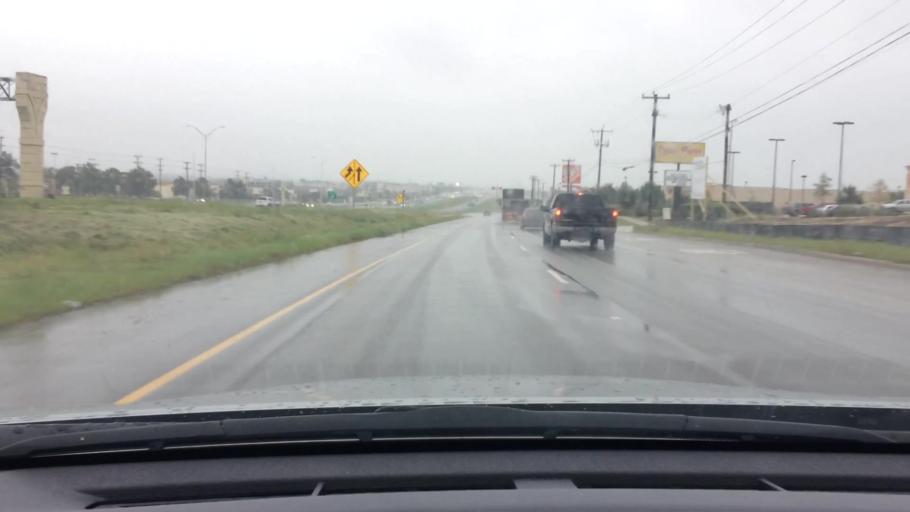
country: US
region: Texas
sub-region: Bexar County
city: Leon Valley
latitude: 29.4872
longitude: -98.7077
